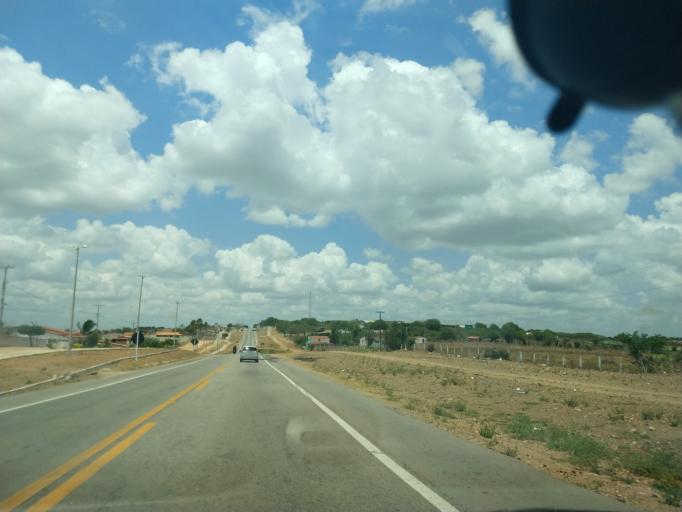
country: BR
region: Rio Grande do Norte
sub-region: Tangara
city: Tangara
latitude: -6.1919
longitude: -35.7914
